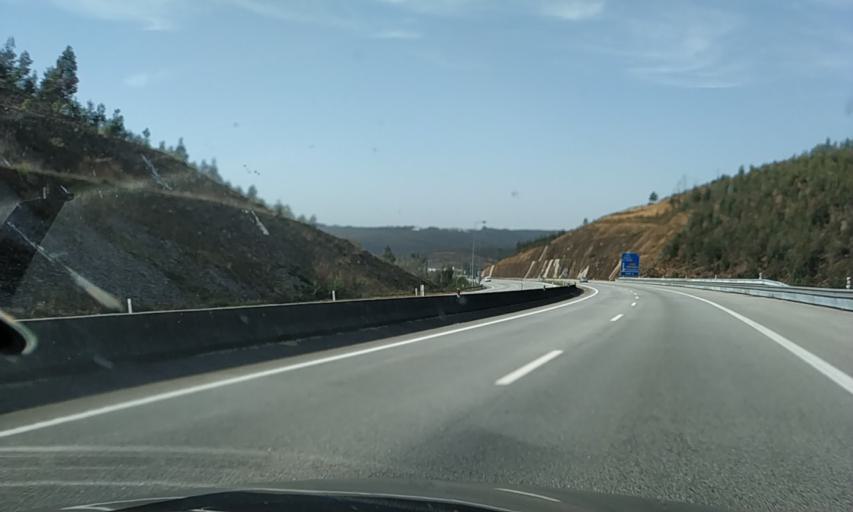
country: PT
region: Aveiro
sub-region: Albergaria-A-Velha
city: Albergaria-a-Velha
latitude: 40.6738
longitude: -8.4282
